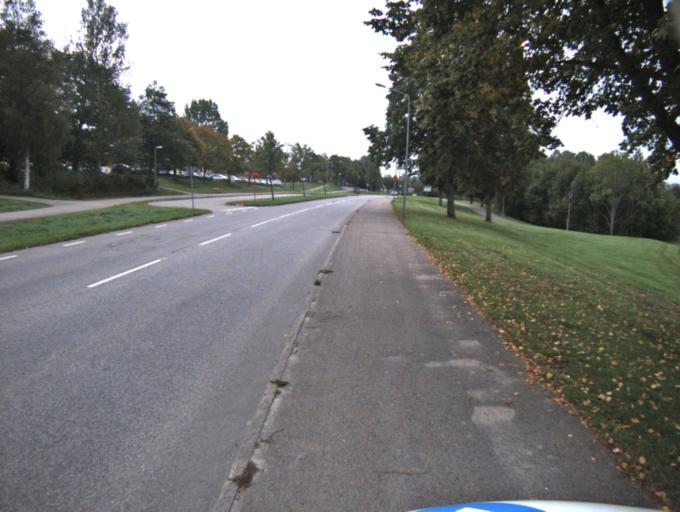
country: SE
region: Vaestra Goetaland
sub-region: Ulricehamns Kommun
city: Ulricehamn
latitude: 57.7910
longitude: 13.4261
